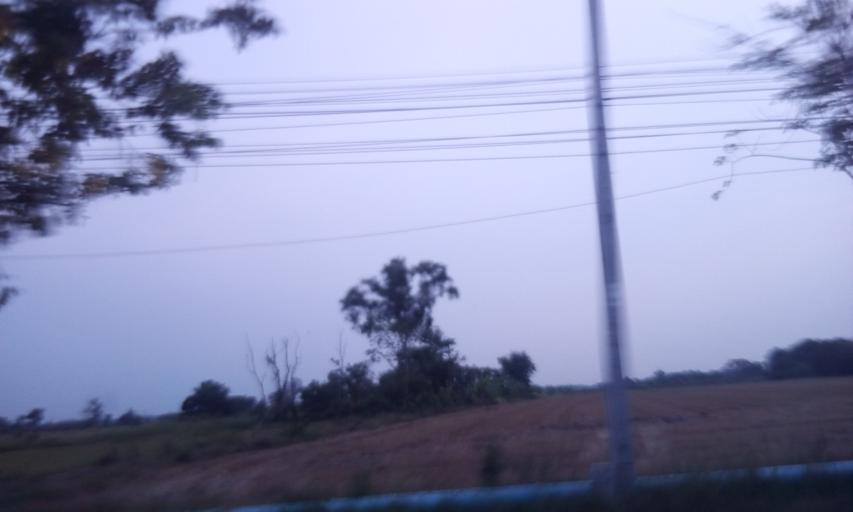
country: TH
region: Bangkok
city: Nong Chok
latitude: 13.8239
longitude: 100.9222
